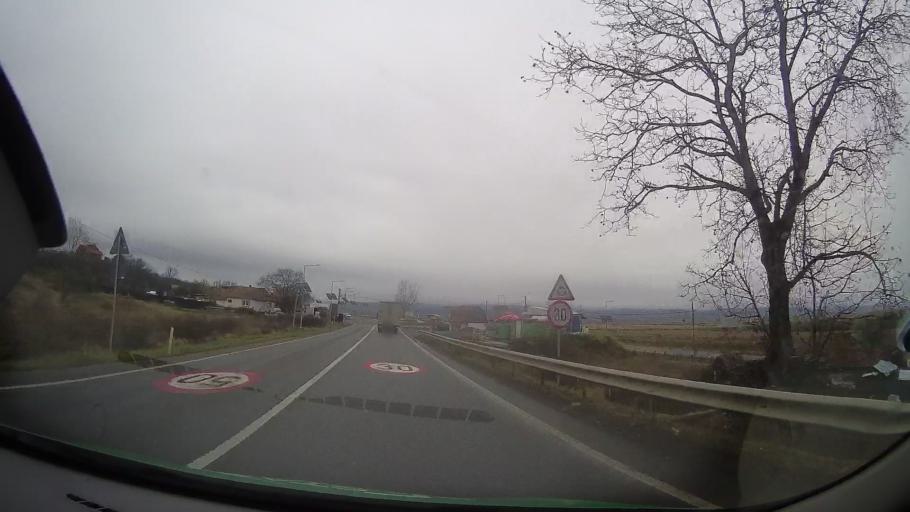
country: RO
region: Mures
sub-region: Comuna Breaza
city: Breaza
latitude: 46.7608
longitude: 24.6623
